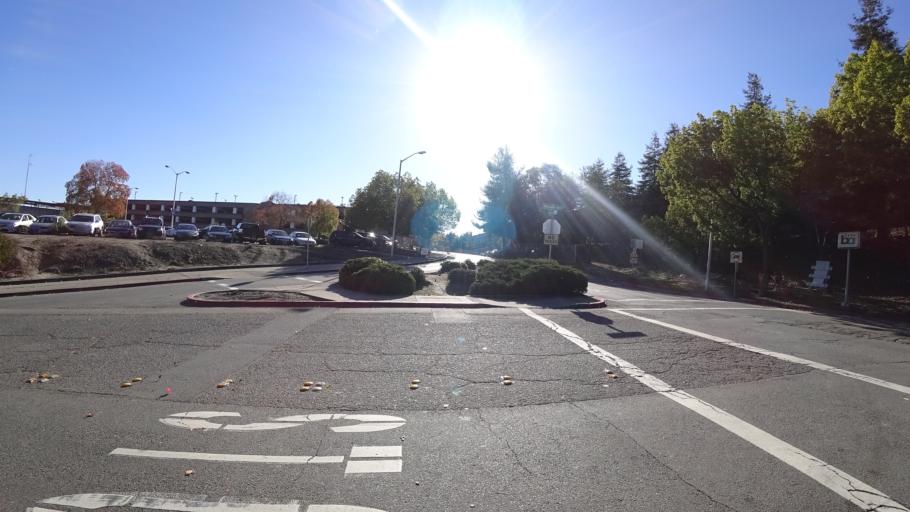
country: US
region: California
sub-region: Contra Costa County
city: Walnut Creek
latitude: 37.9075
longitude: -122.0683
